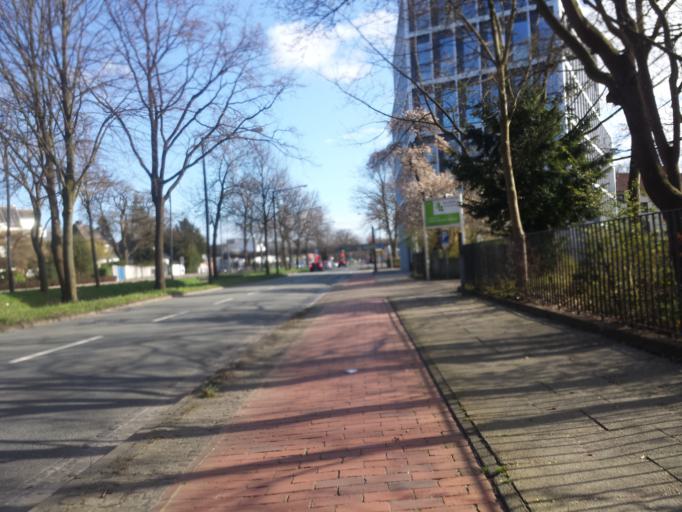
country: DE
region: Lower Saxony
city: Lilienthal
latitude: 53.0839
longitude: 8.8739
